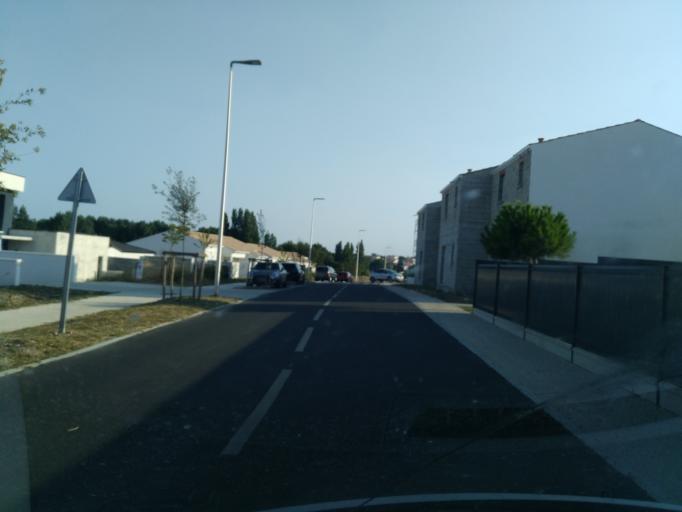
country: FR
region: Poitou-Charentes
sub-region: Departement de la Charente-Maritime
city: Vaux-sur-Mer
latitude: 45.6400
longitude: -1.0539
